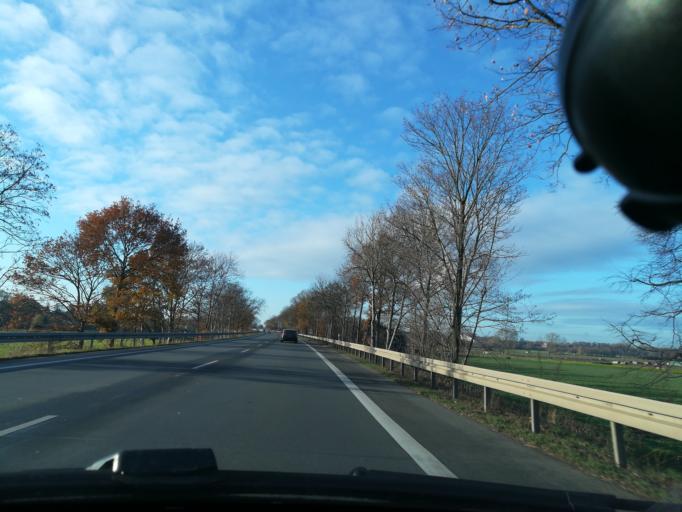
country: DE
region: North Rhine-Westphalia
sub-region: Regierungsbezirk Detmold
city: Petershagen
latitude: 52.3803
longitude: 8.9821
